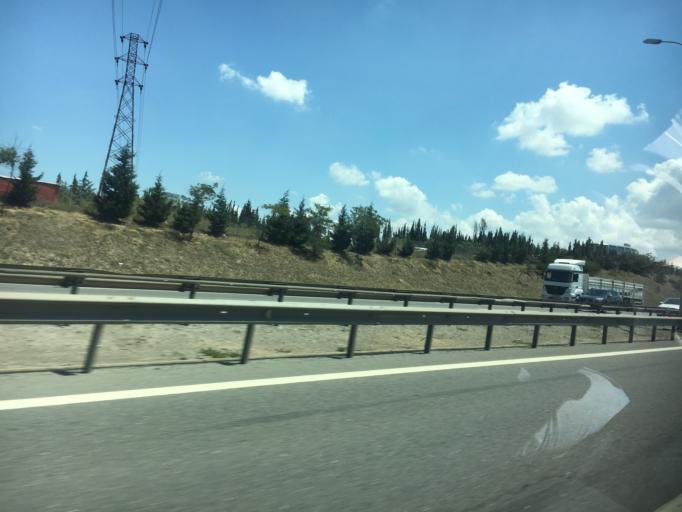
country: TR
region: Kocaeli
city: Balcik
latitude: 40.8888
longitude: 29.3734
